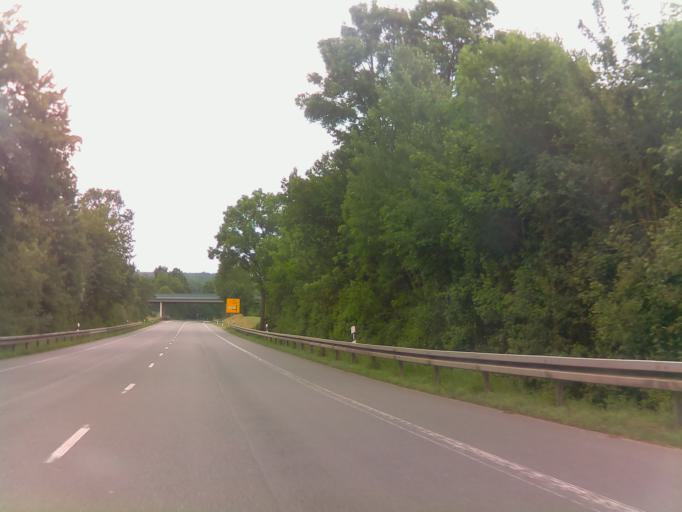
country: DE
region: North Rhine-Westphalia
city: Brakel
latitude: 51.7286
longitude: 9.1679
